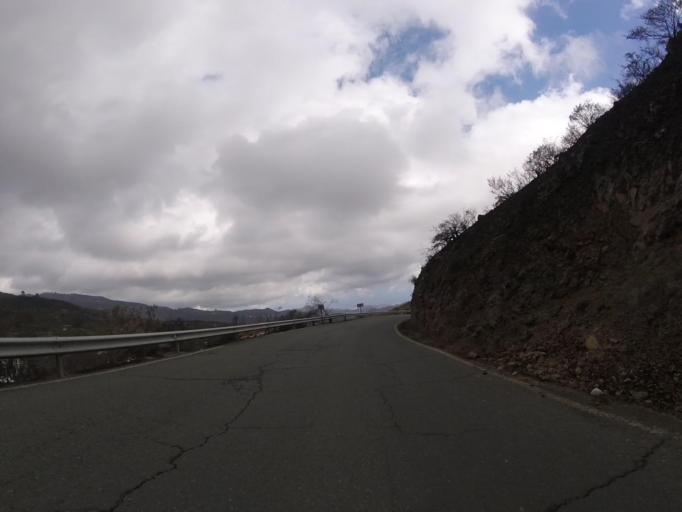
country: ES
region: Canary Islands
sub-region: Provincia de Las Palmas
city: Vega de San Mateo
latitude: 27.9865
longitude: -15.5687
